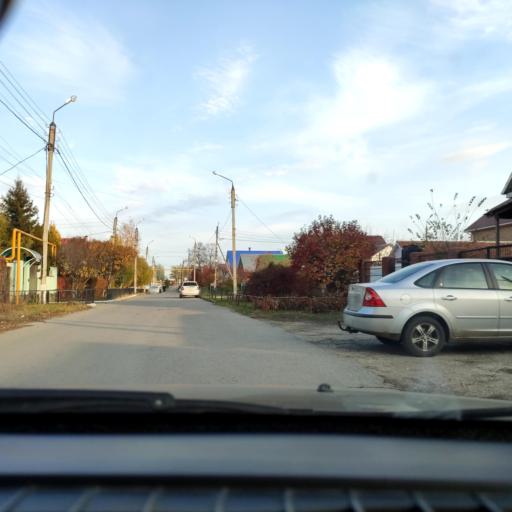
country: RU
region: Samara
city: Tol'yatti
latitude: 53.5374
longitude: 49.3874
